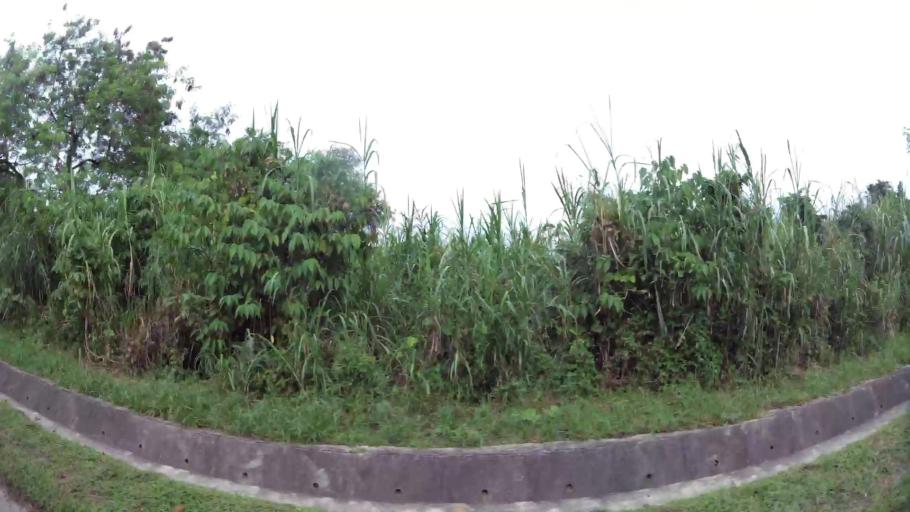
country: MY
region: Johor
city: Johor Bahru
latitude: 1.4175
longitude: 103.7161
